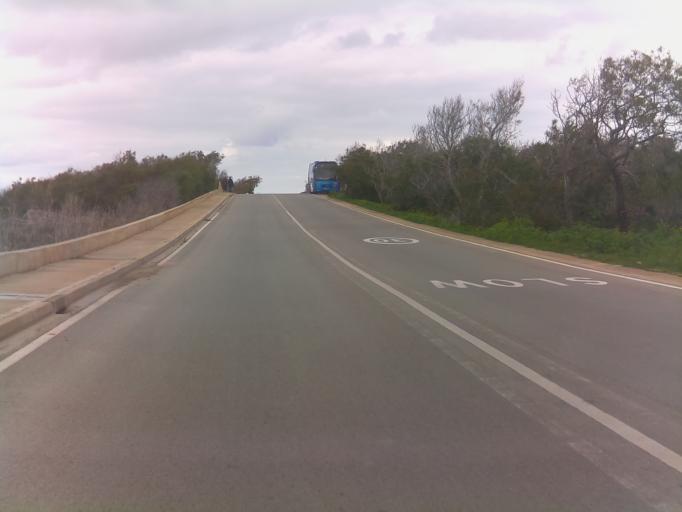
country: MT
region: Il-Mellieha
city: Mellieha
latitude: 35.9775
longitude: 14.3495
